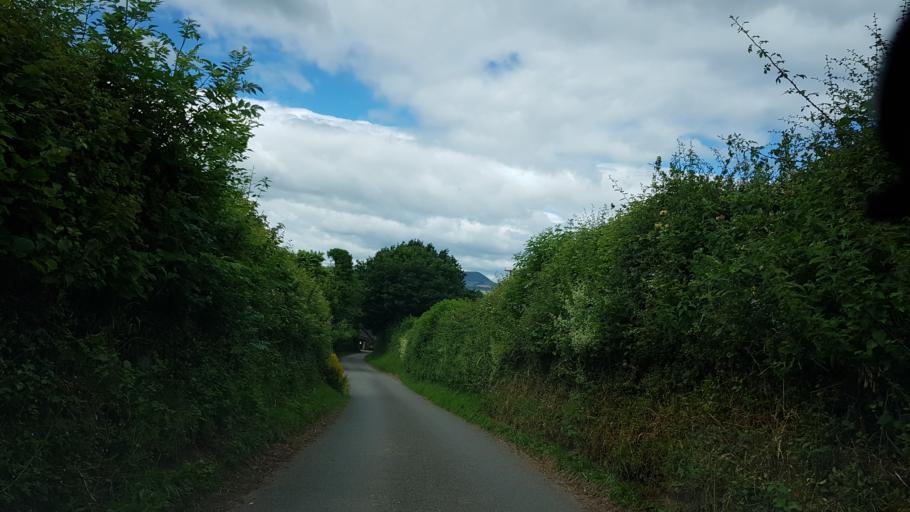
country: GB
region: Wales
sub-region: Monmouthshire
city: Llanarth
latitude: 51.8230
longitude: -2.8669
